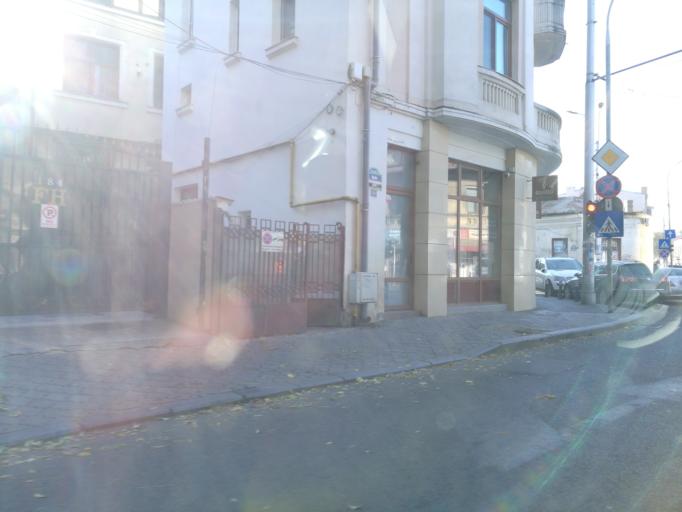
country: RO
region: Bucuresti
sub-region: Municipiul Bucuresti
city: Bucharest
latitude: 44.4467
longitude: 26.1136
